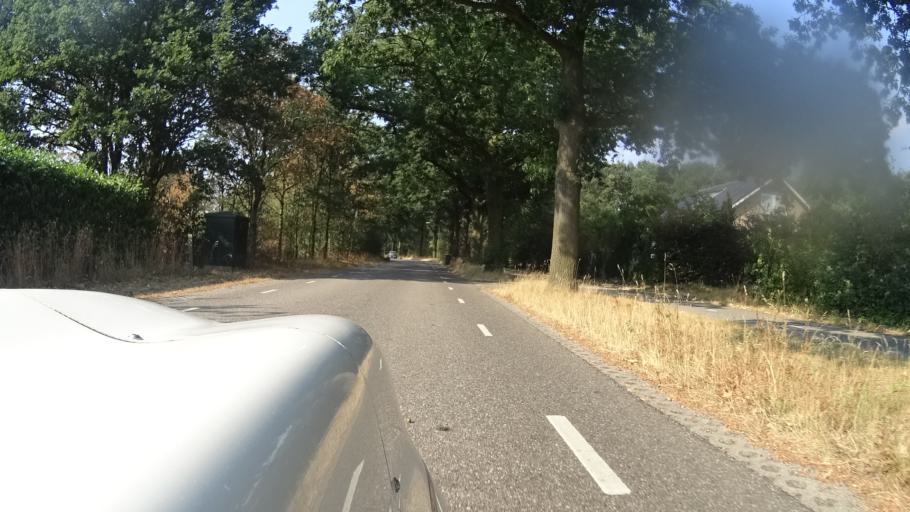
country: NL
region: North Brabant
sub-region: Gemeente Mill en Sint Hubert
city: Wilbertoord
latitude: 51.6622
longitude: 5.7734
